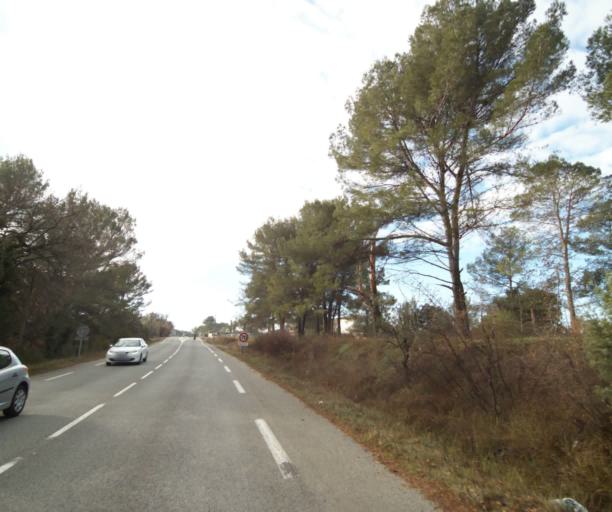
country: FR
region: Provence-Alpes-Cote d'Azur
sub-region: Departement du Var
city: Trans-en-Provence
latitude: 43.4907
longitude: 6.4842
